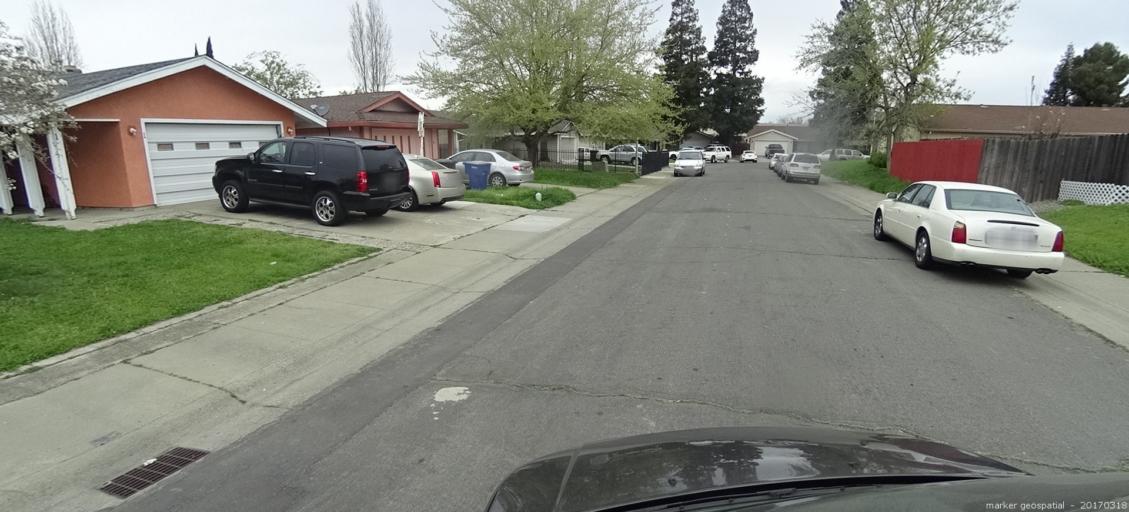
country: US
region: California
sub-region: Sacramento County
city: Parkway
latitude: 38.4761
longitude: -121.4556
